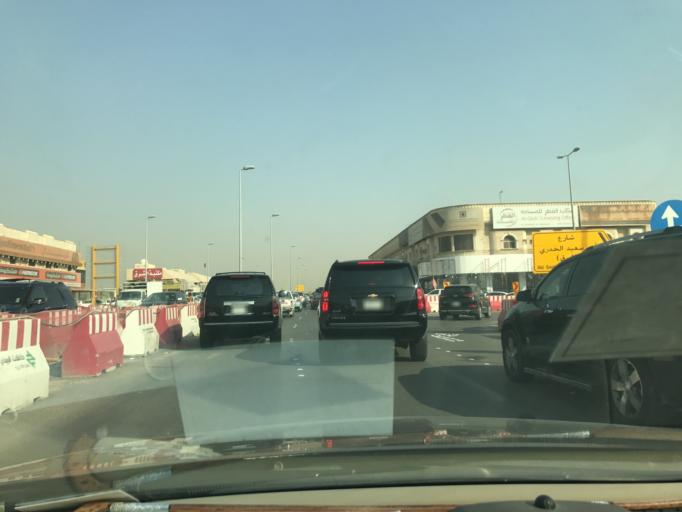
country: SA
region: Ar Riyad
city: Riyadh
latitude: 24.7540
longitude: 46.7695
